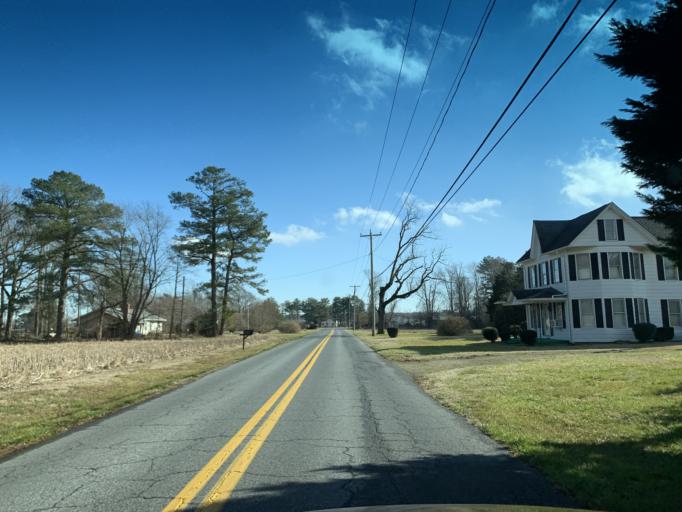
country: US
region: Delaware
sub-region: Sussex County
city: Selbyville
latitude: 38.4538
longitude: -75.1999
